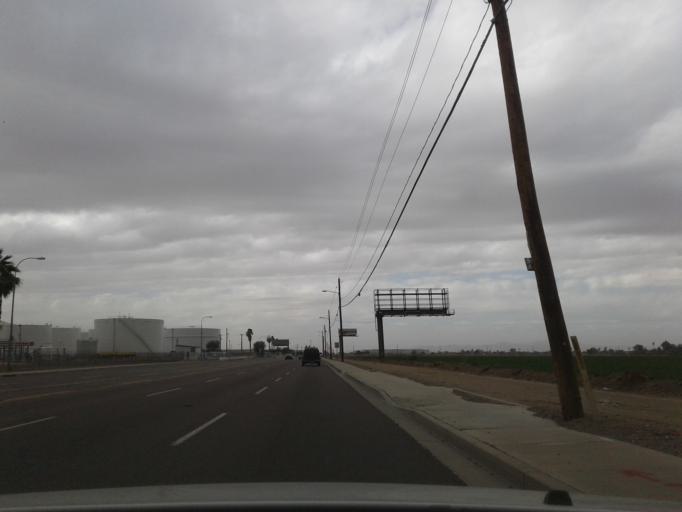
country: US
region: Arizona
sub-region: Maricopa County
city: Tolleson
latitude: 33.4513
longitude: -112.1741
